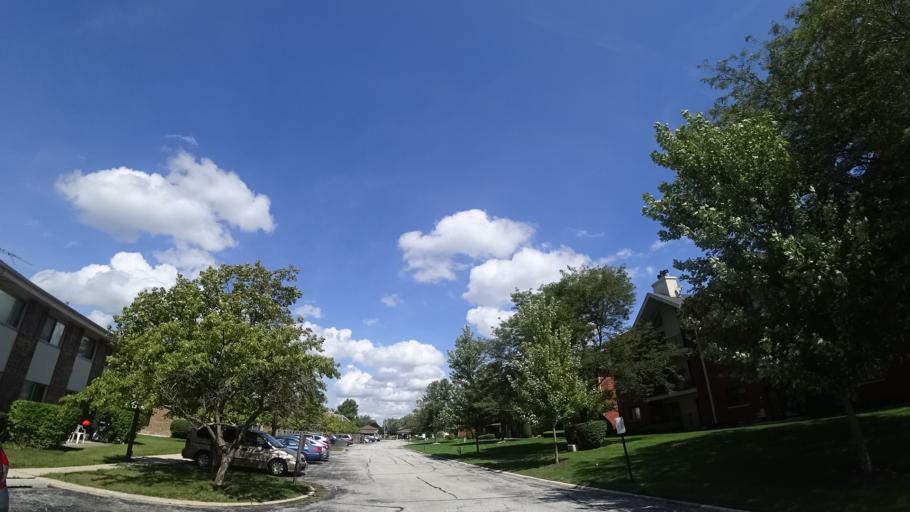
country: US
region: Illinois
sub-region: Cook County
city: Tinley Park
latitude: 41.5611
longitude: -87.7787
